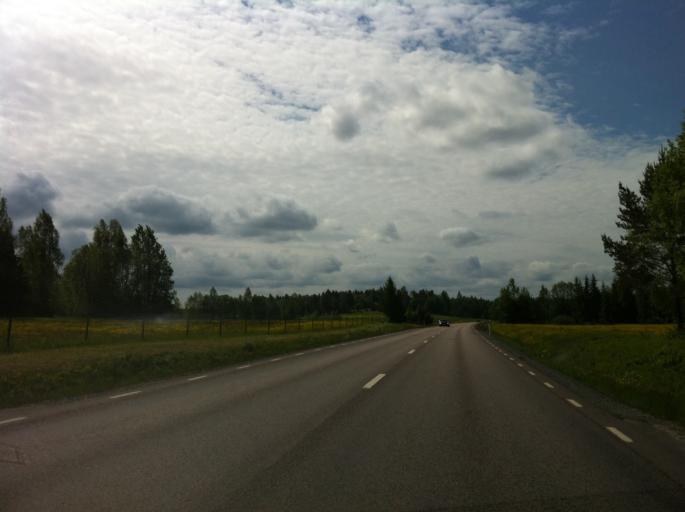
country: SE
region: Vaermland
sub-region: Karlstads Kommun
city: Edsvalla
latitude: 59.4650
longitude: 13.2150
